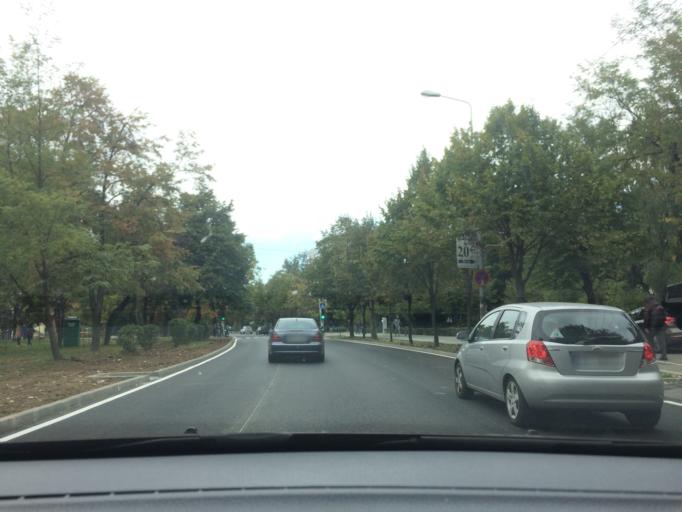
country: RO
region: Timis
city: Timisoara
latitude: 45.7476
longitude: 21.2399
